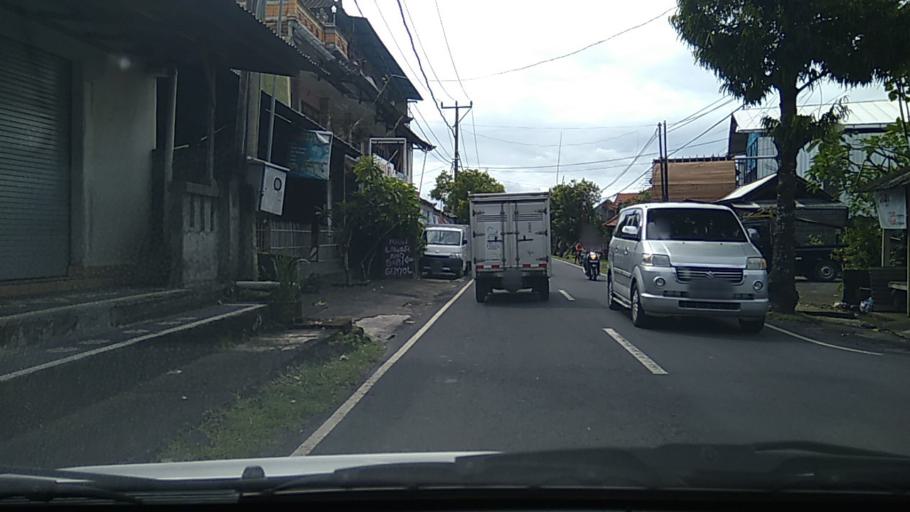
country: ID
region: Bali
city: Banjar Sedang
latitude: -8.5681
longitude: 115.2553
